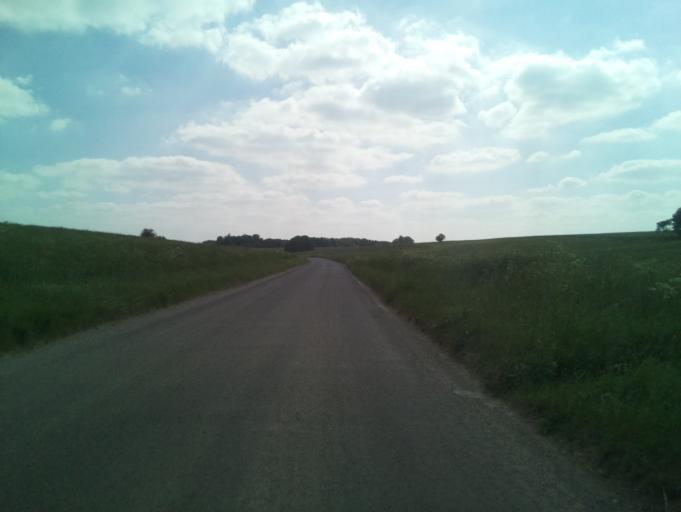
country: GB
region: England
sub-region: Wiltshire
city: Tidworth
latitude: 51.2657
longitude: -1.7235
